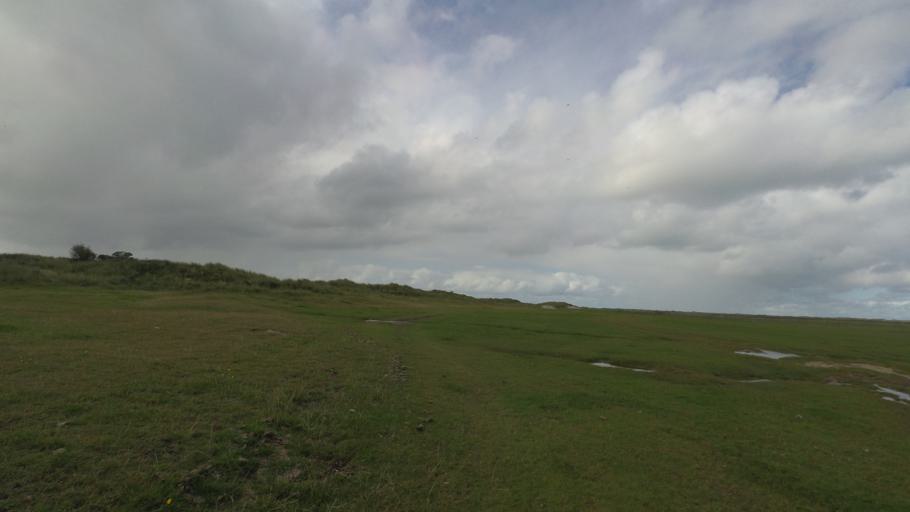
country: NL
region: Friesland
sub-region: Gemeente Ameland
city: Nes
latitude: 53.4495
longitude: 5.8620
